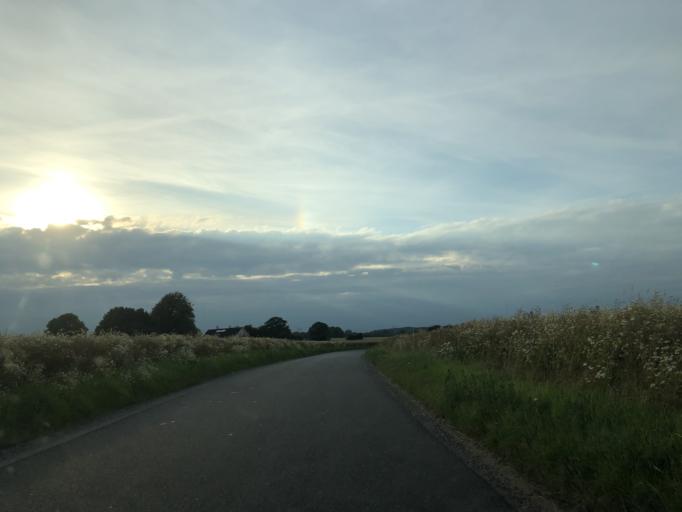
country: DK
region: South Denmark
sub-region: Vejle Kommune
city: Borkop
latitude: 55.6179
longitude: 9.6021
